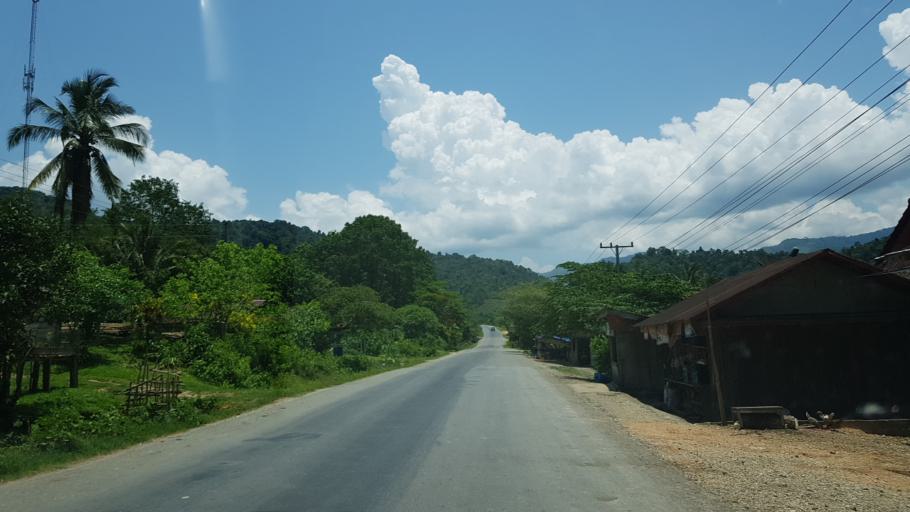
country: LA
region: Vientiane
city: Muang Kasi
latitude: 19.1318
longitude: 102.2248
